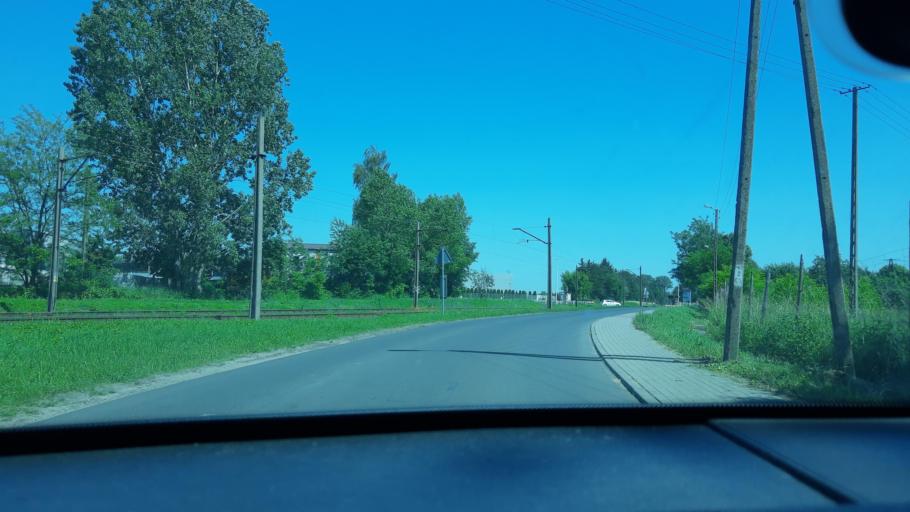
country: PL
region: Lodz Voivodeship
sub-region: Powiat zdunskowolski
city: Zdunska Wola
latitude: 51.6216
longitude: 18.9631
